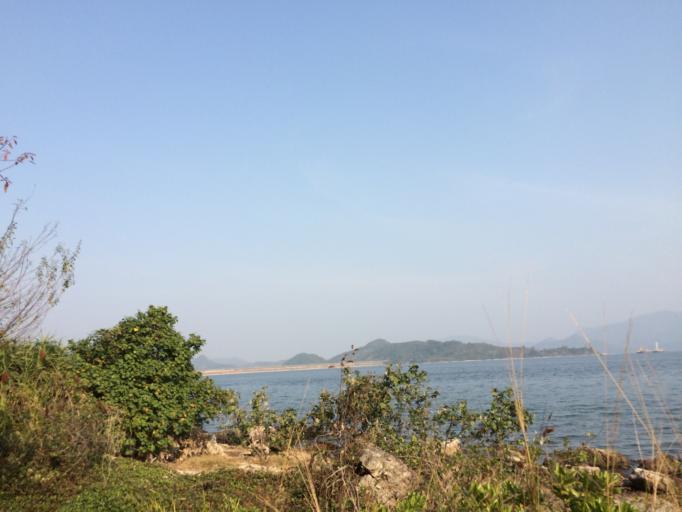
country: HK
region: Tai Po
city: Tai Po
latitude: 22.4519
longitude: 114.2305
